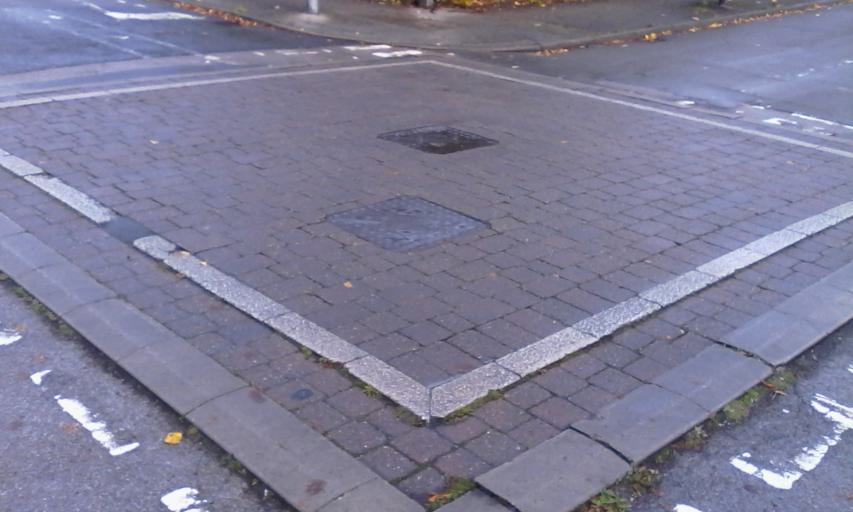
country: GB
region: England
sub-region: Nottinghamshire
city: Arnold
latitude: 52.9820
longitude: -1.1175
